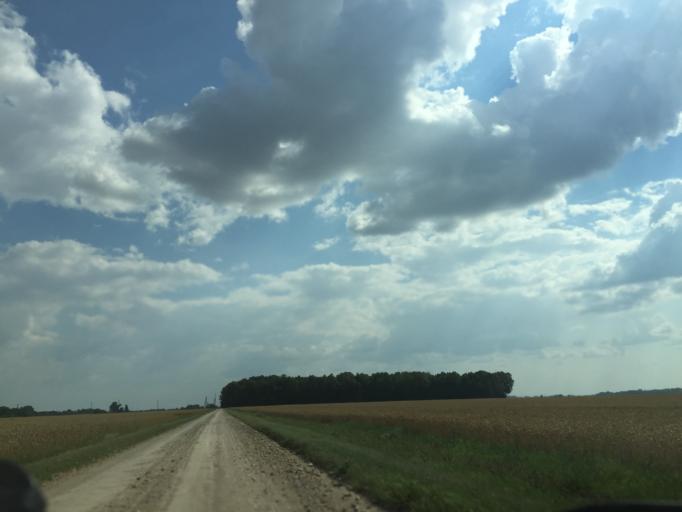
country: LV
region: Jelgava
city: Jelgava
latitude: 56.4889
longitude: 23.7597
